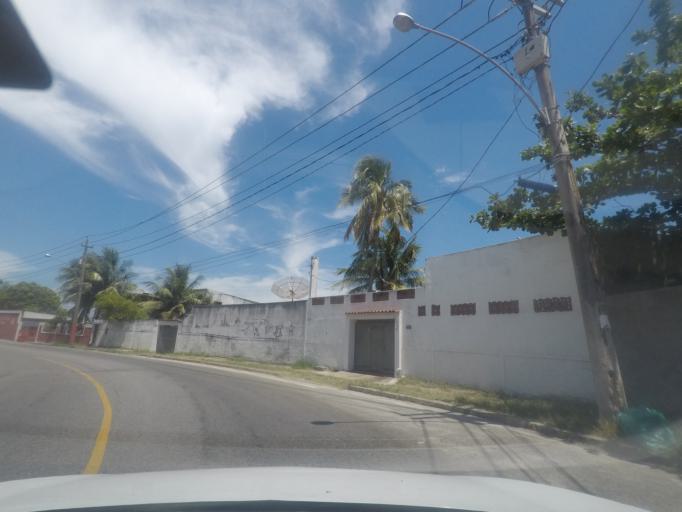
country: BR
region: Rio de Janeiro
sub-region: Itaguai
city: Itaguai
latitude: -22.9858
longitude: -43.7000
